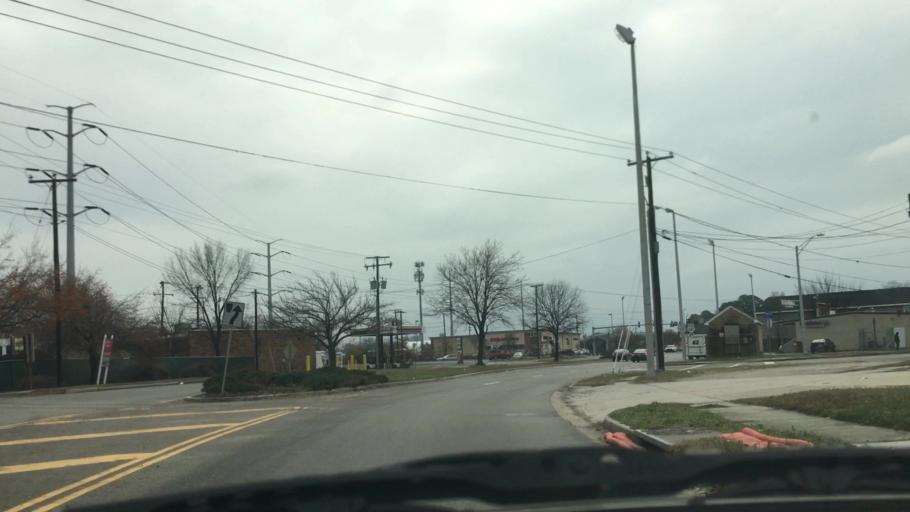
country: US
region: Virginia
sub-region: City of Norfolk
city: Norfolk
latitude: 36.8777
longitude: -76.2524
